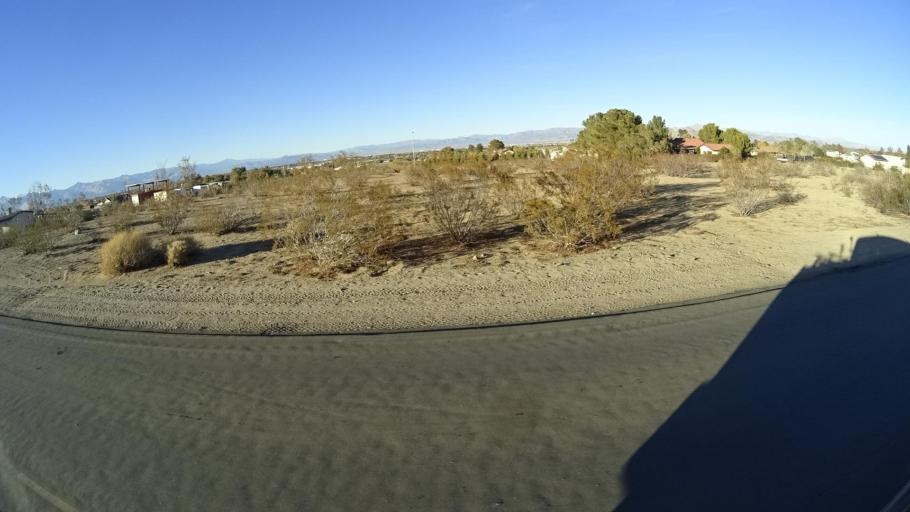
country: US
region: California
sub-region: Kern County
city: Ridgecrest
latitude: 35.5860
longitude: -117.6592
